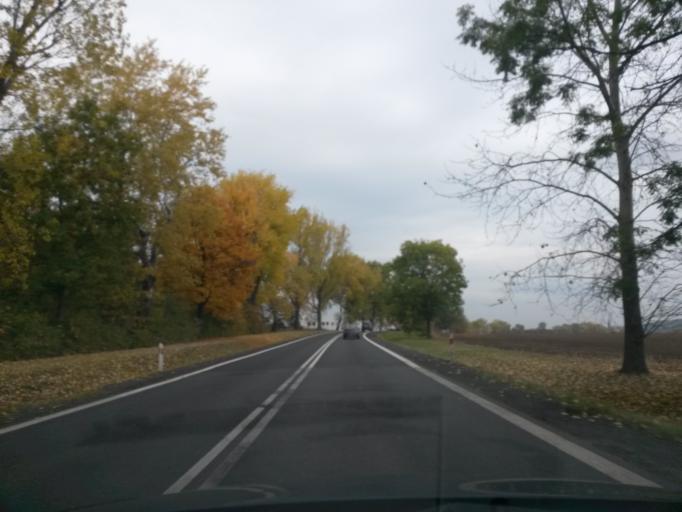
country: PL
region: Lower Silesian Voivodeship
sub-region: Powiat dzierzoniowski
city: Niemcza
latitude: 50.6967
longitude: 16.8220
